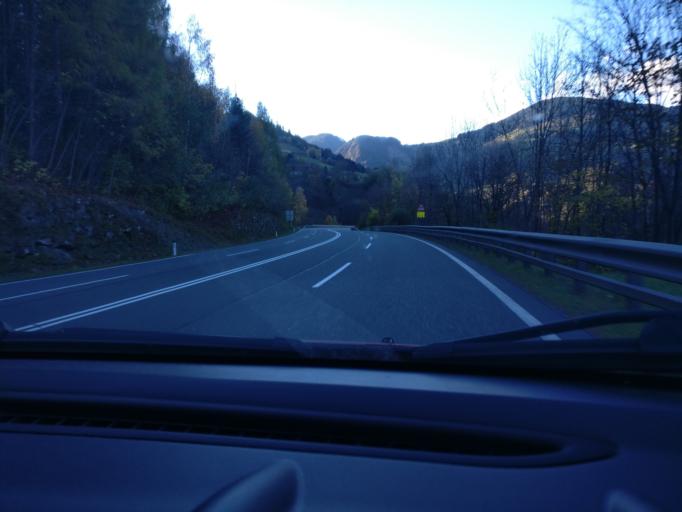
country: AT
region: Salzburg
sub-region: Politischer Bezirk Zell am See
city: Lend
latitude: 47.2959
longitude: 13.0465
